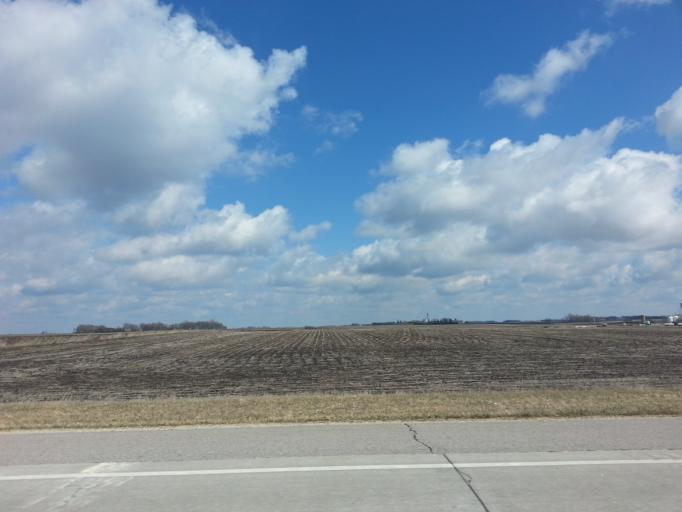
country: US
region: Minnesota
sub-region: Dodge County
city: Dodge Center
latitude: 44.1210
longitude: -92.8995
